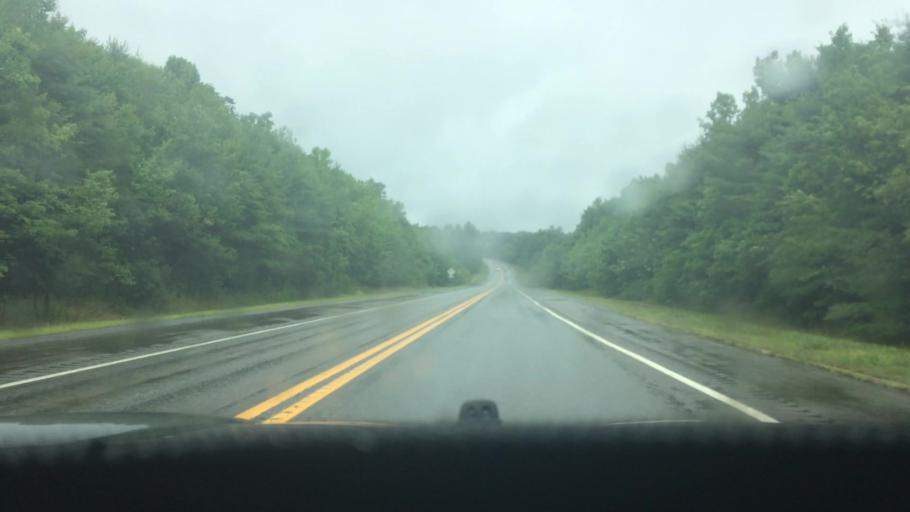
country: US
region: Massachusetts
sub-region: Worcester County
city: South Ashburnham
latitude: 42.5779
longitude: -71.9512
